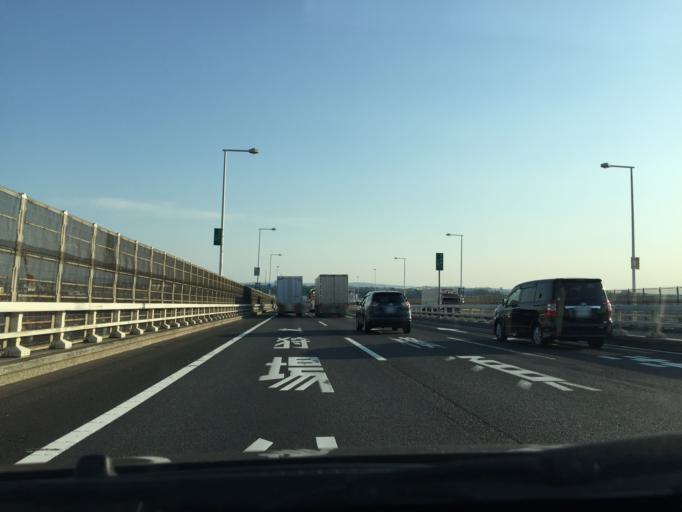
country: JP
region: Kanagawa
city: Yokohama
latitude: 35.4498
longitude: 139.6709
